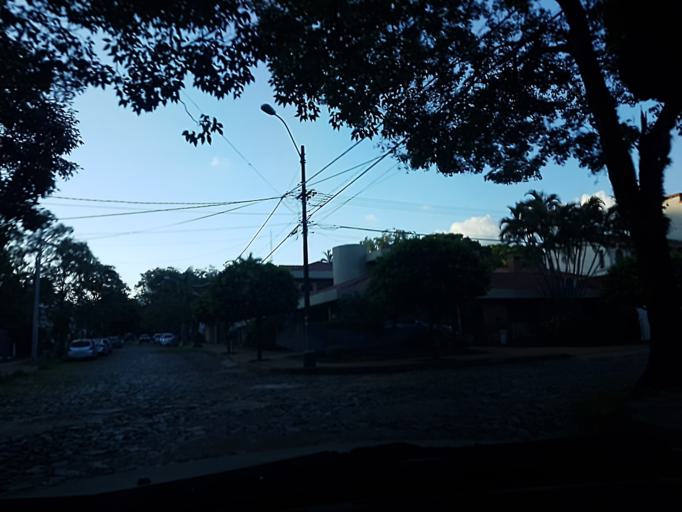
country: PY
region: Asuncion
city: Asuncion
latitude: -25.3005
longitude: -57.6007
